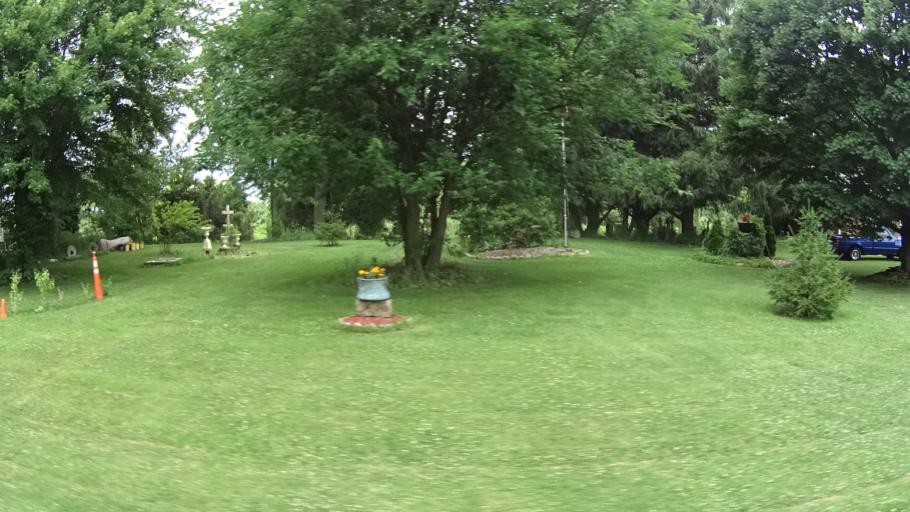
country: US
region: Ohio
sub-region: Lorain County
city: Vermilion
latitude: 41.3686
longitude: -82.3691
